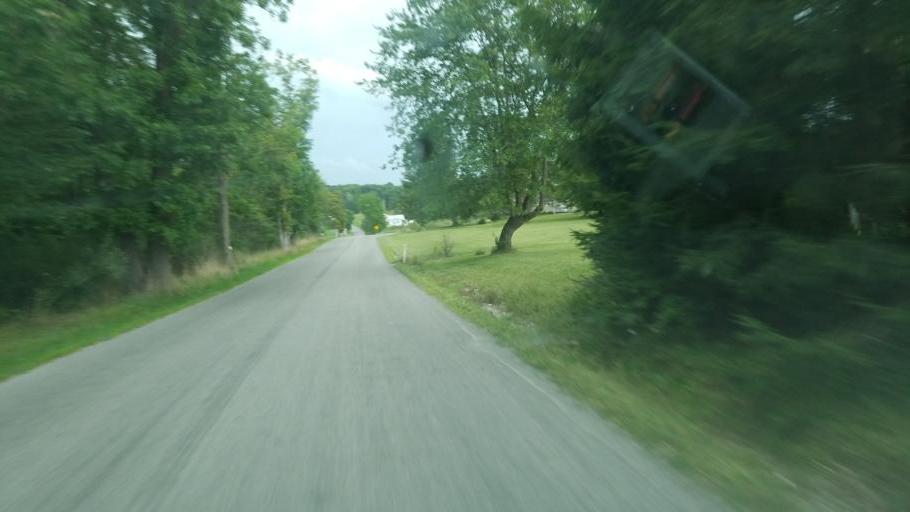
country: US
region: Pennsylvania
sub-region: Clarion County
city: Knox
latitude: 41.1582
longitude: -79.5315
